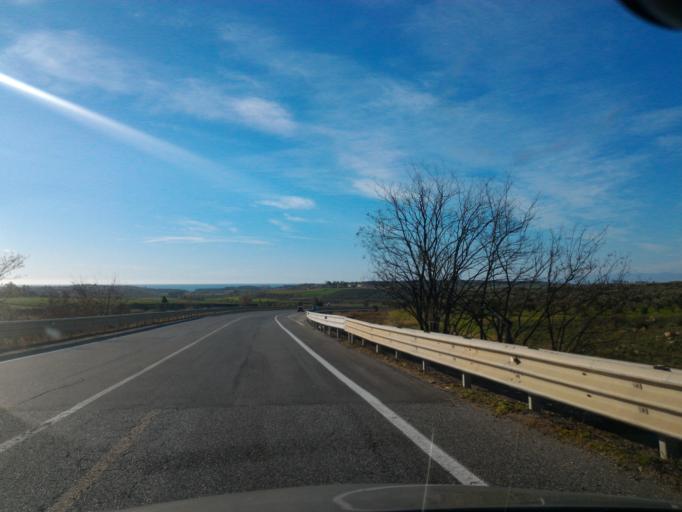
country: IT
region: Calabria
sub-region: Provincia di Crotone
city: Isola di Capo Rizzuto
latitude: 38.9439
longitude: 17.0808
